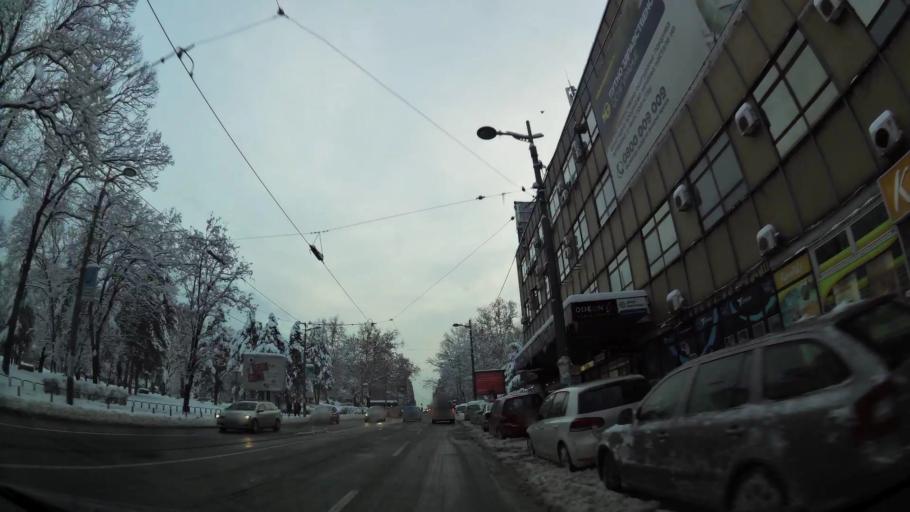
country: RS
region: Central Serbia
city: Belgrade
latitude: 44.8089
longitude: 20.4737
